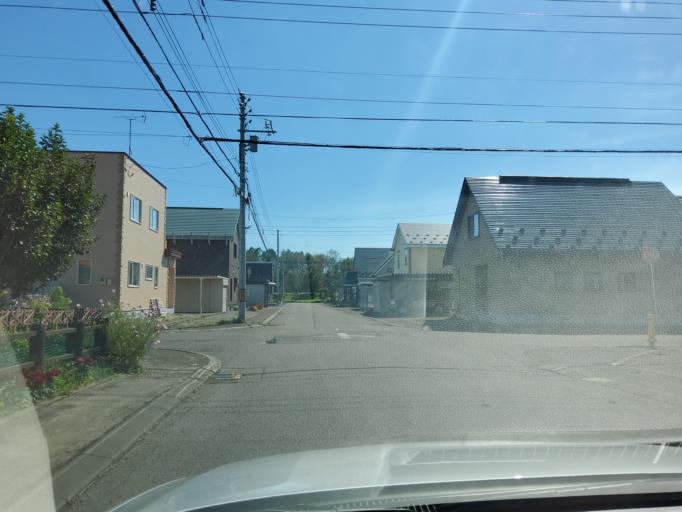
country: JP
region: Hokkaido
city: Obihiro
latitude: 42.9405
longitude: 143.2200
